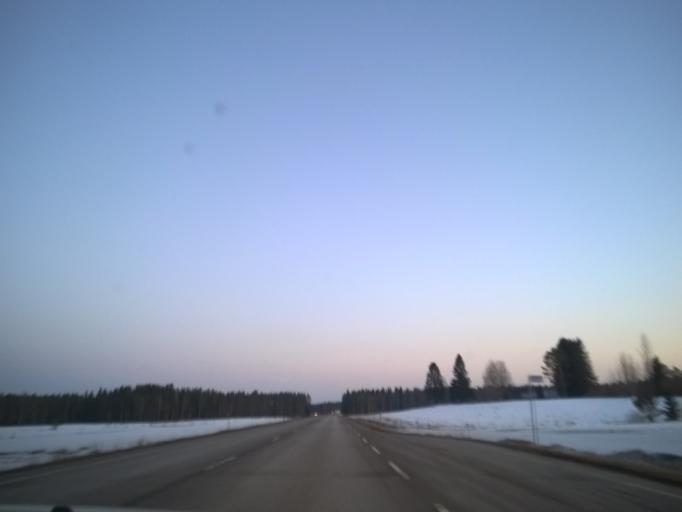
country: FI
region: Northern Ostrobothnia
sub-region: Nivala-Haapajaervi
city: Pyhaejaervi
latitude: 63.8000
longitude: 25.9158
